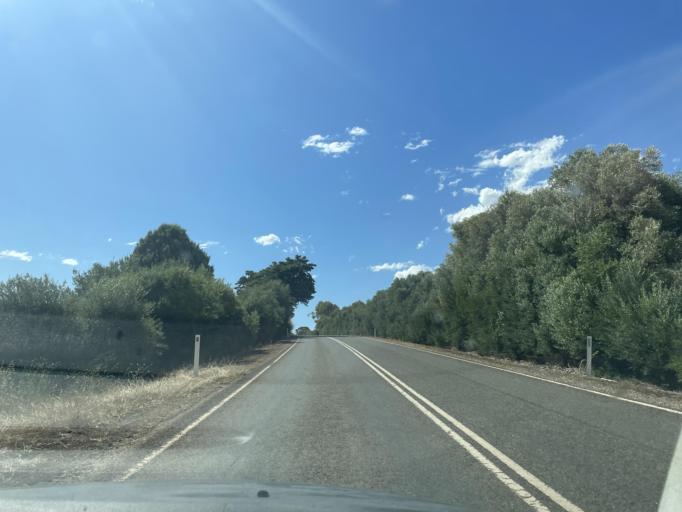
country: AU
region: South Australia
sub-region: Clare and Gilbert Valleys
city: Clare
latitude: -33.9107
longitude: 138.7156
